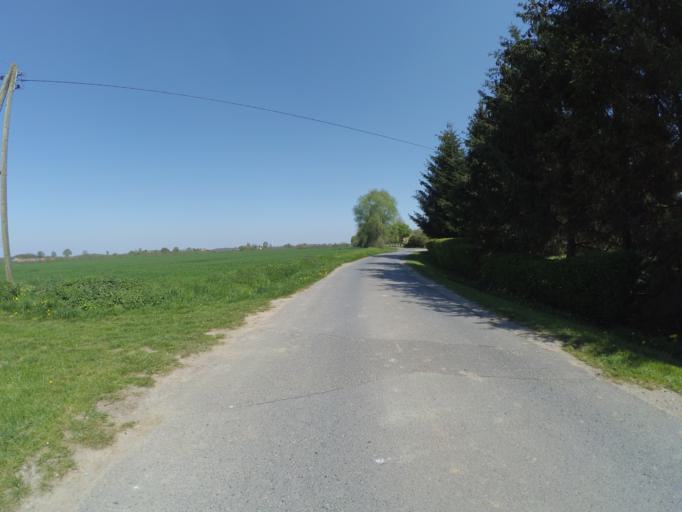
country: DE
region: North Rhine-Westphalia
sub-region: Regierungsbezirk Munster
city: Nordkirchen
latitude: 51.7690
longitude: 7.5495
